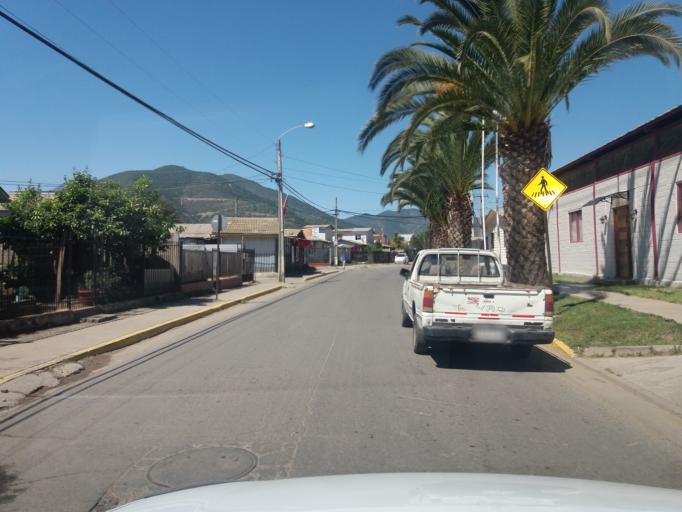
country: CL
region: Valparaiso
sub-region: Provincia de Quillota
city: Quillota
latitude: -32.9398
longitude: -71.2747
